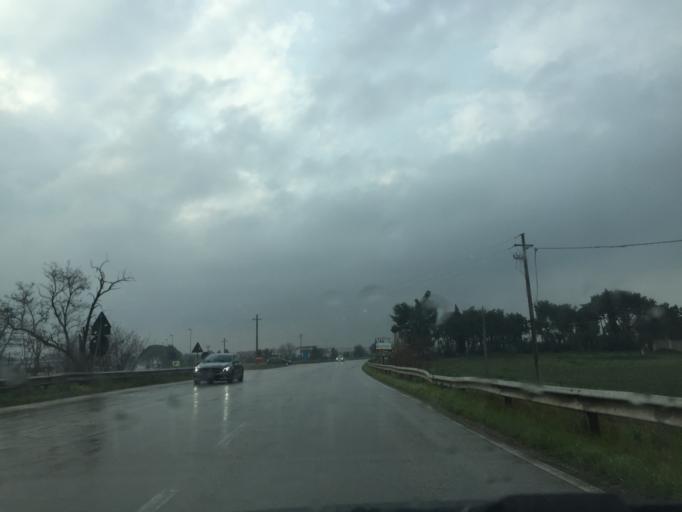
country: IT
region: Apulia
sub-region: Provincia di Foggia
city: Foggia
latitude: 41.4920
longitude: 15.5225
